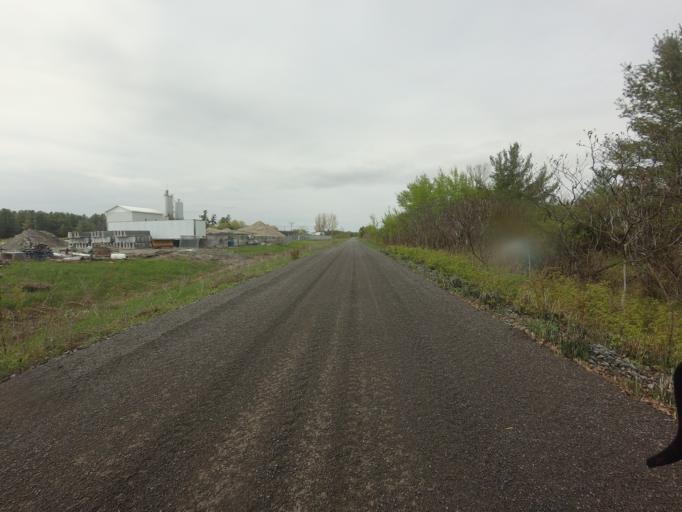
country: CA
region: Ontario
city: Carleton Place
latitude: 45.1539
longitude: -76.1441
